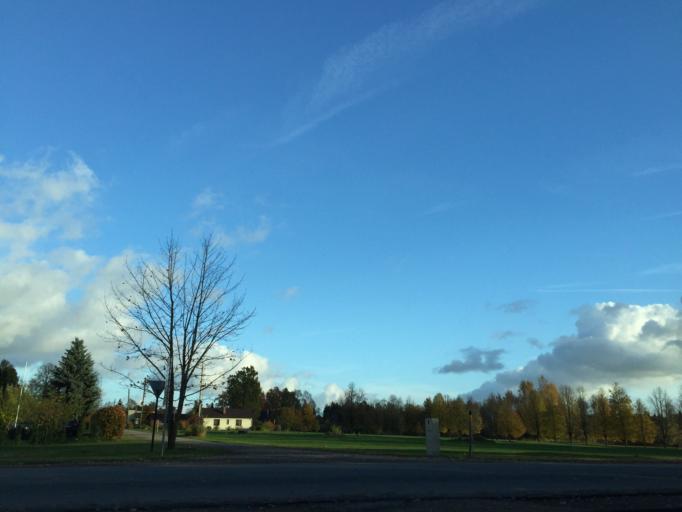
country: LV
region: Ogre
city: Jumprava
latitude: 56.7688
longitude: 25.0007
